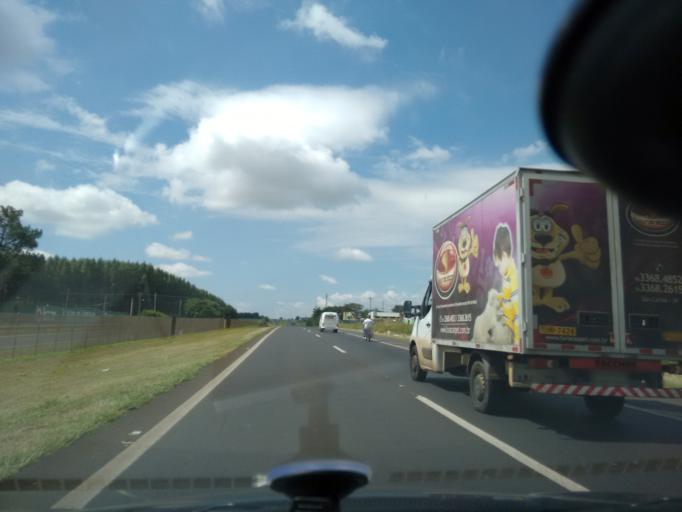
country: BR
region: Sao Paulo
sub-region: Ibate
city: Ibate
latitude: -21.9437
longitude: -48.0025
